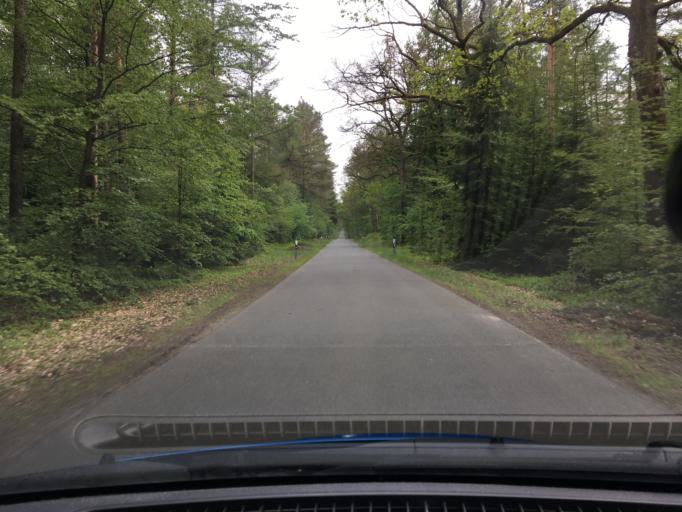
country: DE
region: Lower Saxony
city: Eimke
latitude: 52.9780
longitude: 10.2493
